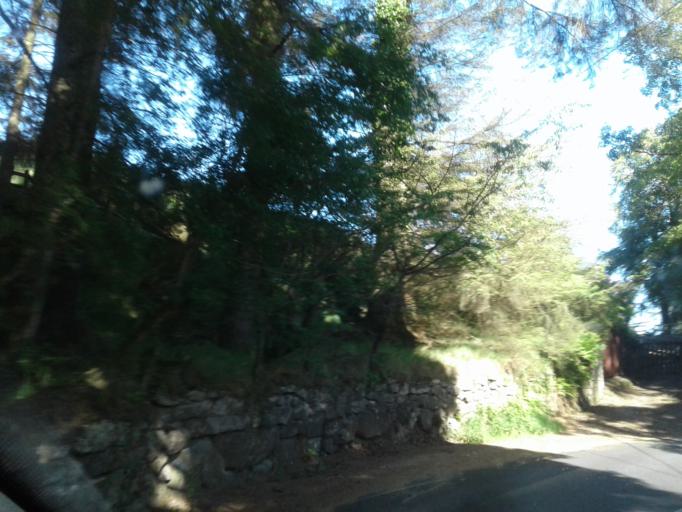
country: IE
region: Leinster
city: Ballinteer
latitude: 53.2006
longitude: -6.2922
